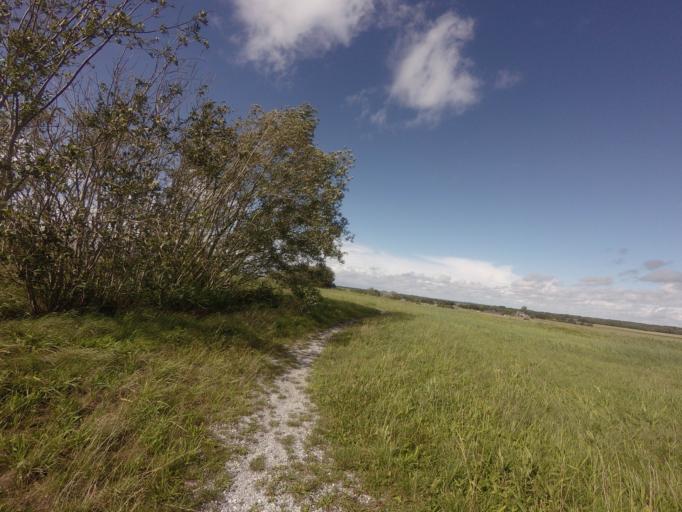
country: NL
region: Groningen
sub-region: Gemeente Leek
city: Leek
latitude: 53.0135
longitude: 6.3395
